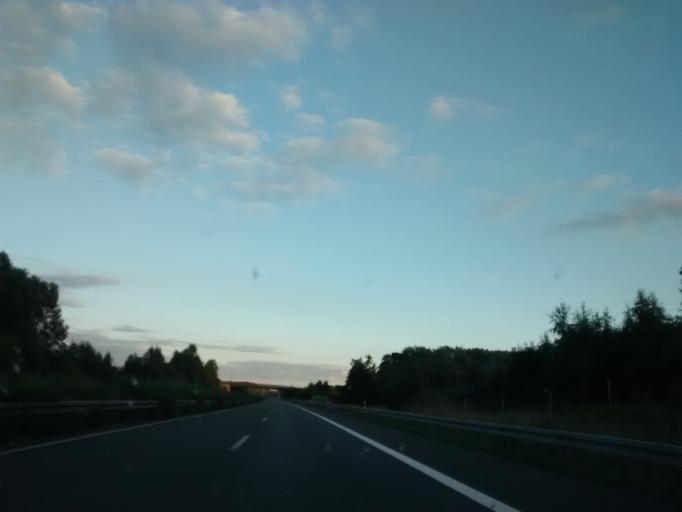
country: DE
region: Lower Saxony
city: Dissen
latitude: 52.0994
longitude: 8.2000
